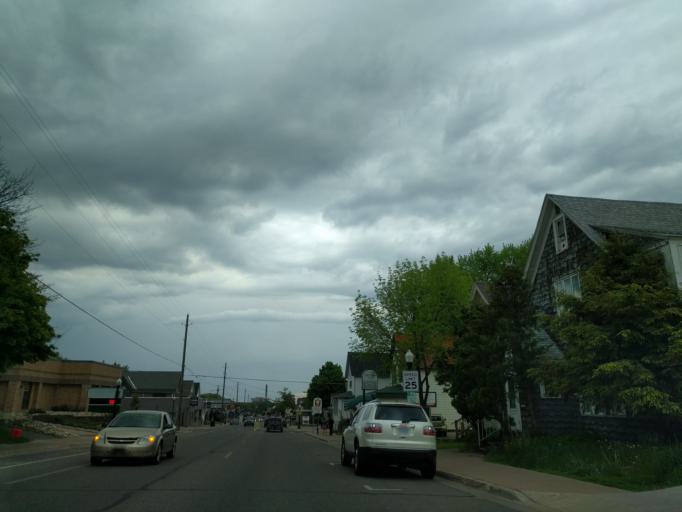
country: US
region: Michigan
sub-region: Marquette County
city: Marquette
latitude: 46.5505
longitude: -87.3947
